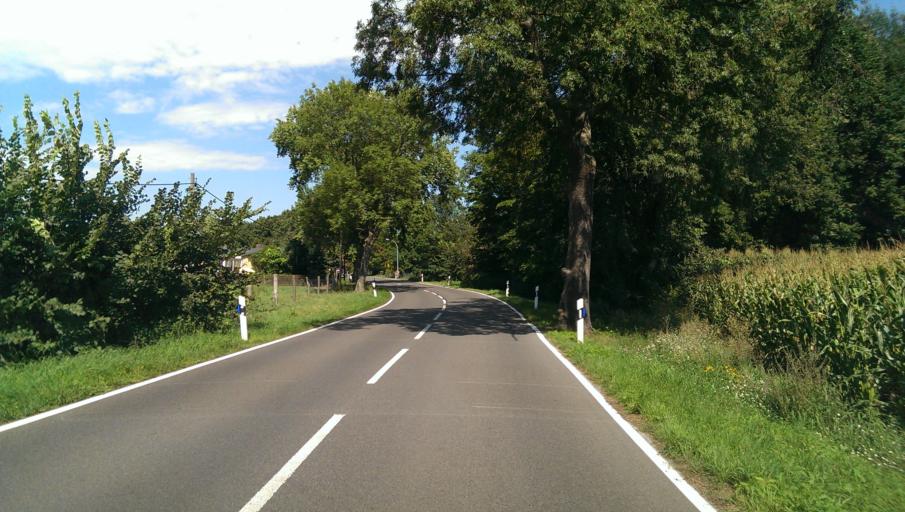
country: DE
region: Brandenburg
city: Trebbin
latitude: 52.2543
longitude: 13.2061
